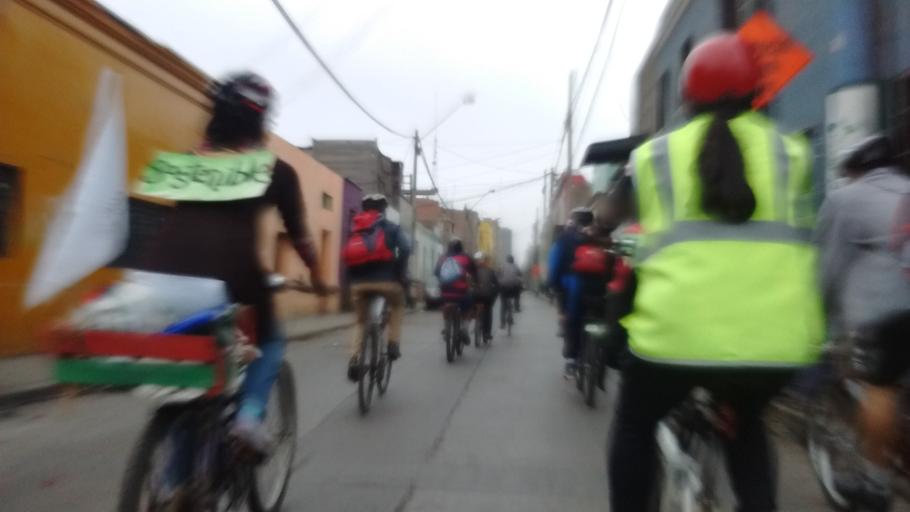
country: PE
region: Lima
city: Lima
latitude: -12.0657
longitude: -77.0282
